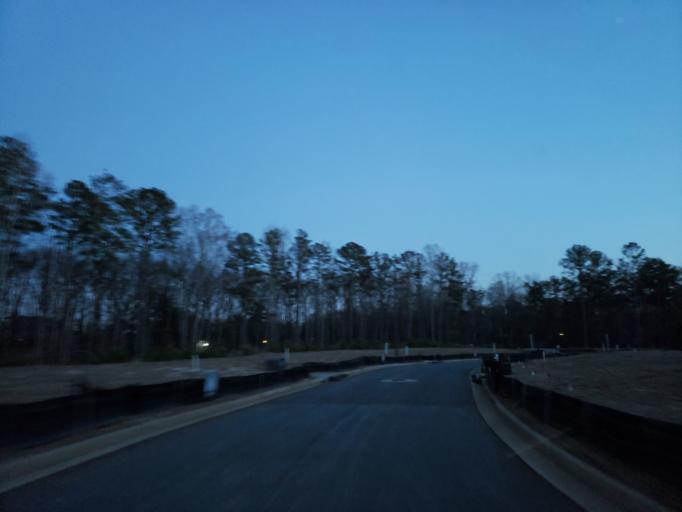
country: US
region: Georgia
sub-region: Cobb County
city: Powder Springs
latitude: 33.9323
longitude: -84.6948
